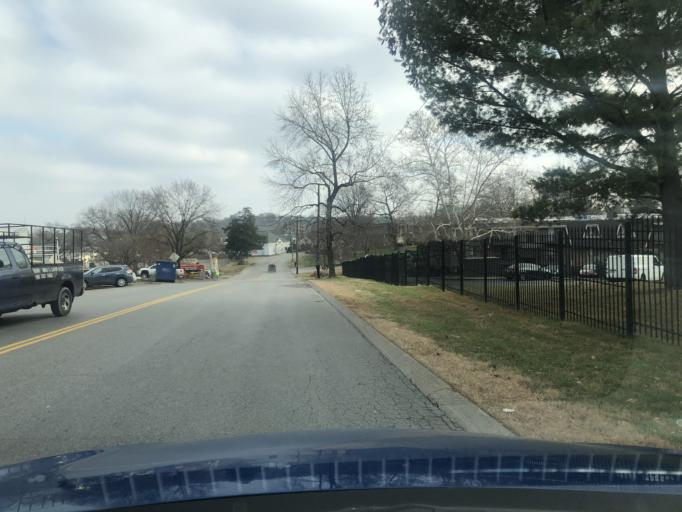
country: US
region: Tennessee
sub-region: Davidson County
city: Oak Hill
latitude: 36.0835
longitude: -86.7054
